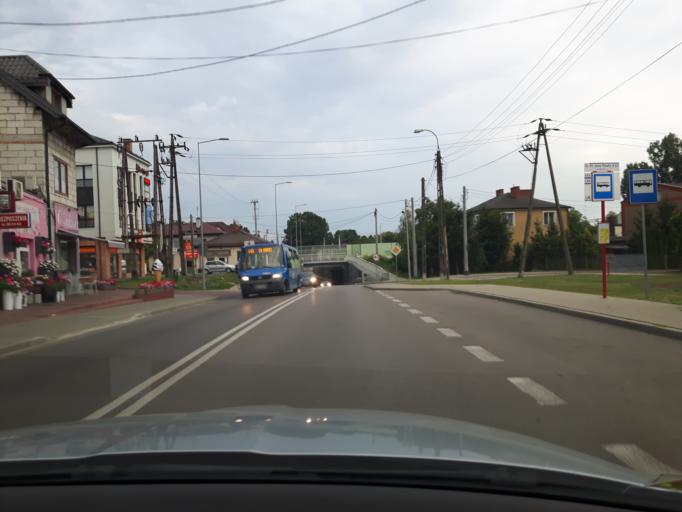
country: PL
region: Masovian Voivodeship
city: Zielonka
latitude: 52.3111
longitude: 21.1525
